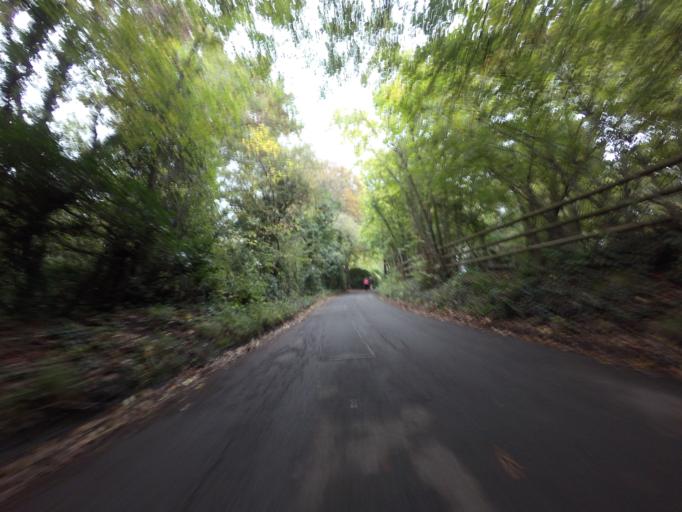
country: GB
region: England
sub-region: Kent
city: Swanley
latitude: 51.3876
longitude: 0.1601
